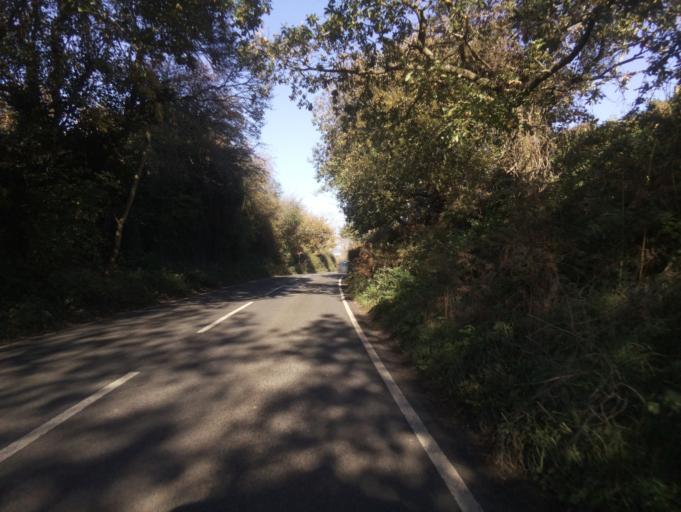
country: GB
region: England
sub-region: Somerset
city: Yeovil
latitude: 50.9292
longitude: -2.6180
